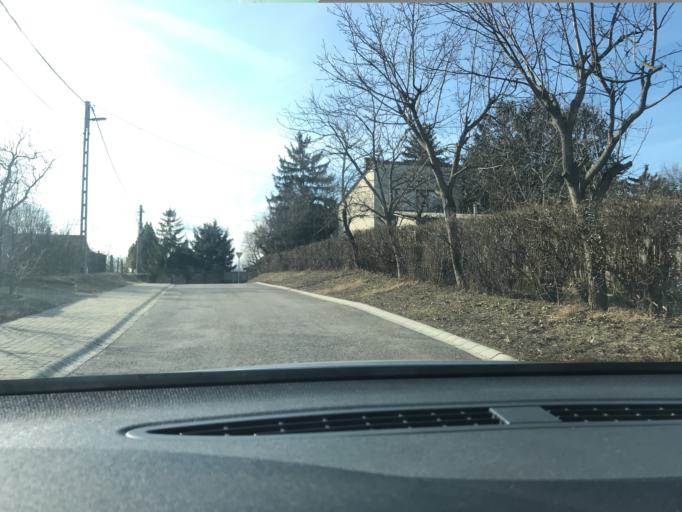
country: HU
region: Pest
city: Fot
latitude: 47.6280
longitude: 19.1732
